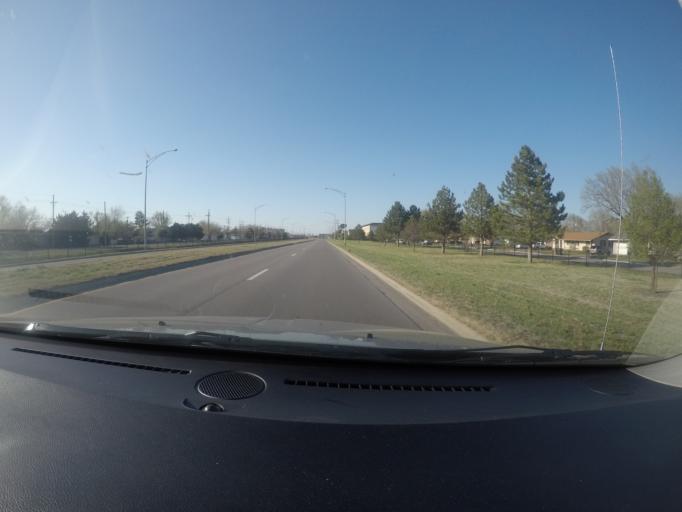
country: US
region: Kansas
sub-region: Reno County
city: Hutchinson
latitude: 38.0612
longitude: -97.9033
